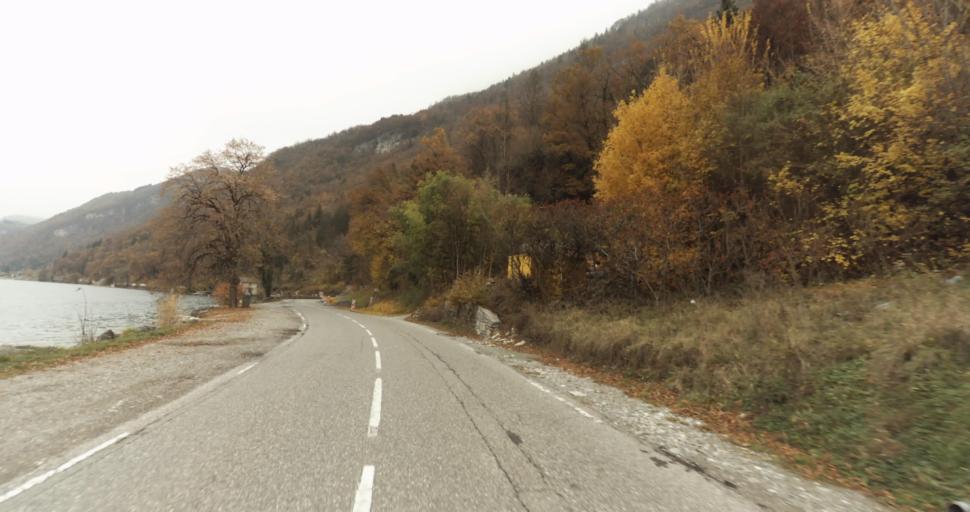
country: FR
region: Rhone-Alpes
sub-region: Departement de la Haute-Savoie
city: Doussard
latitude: 45.8046
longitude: 6.2315
